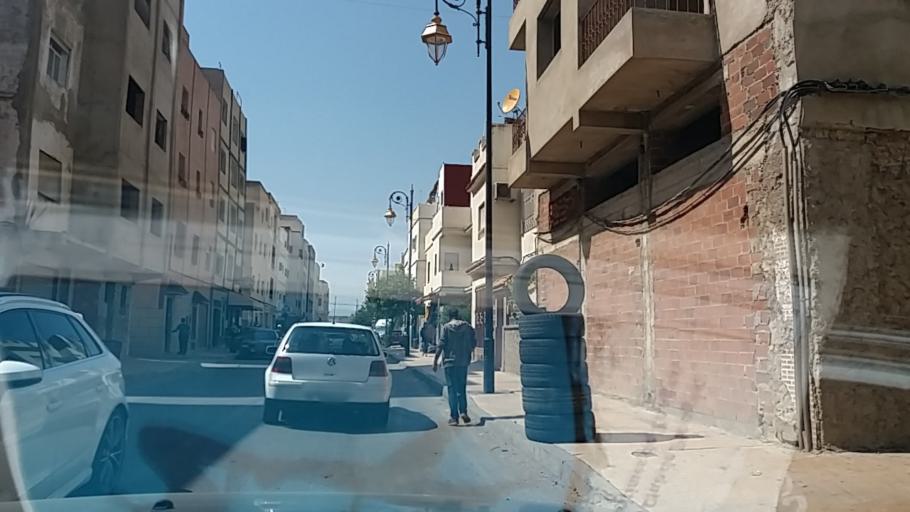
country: MA
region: Tanger-Tetouan
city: Tetouan
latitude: 35.5628
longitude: -5.3659
